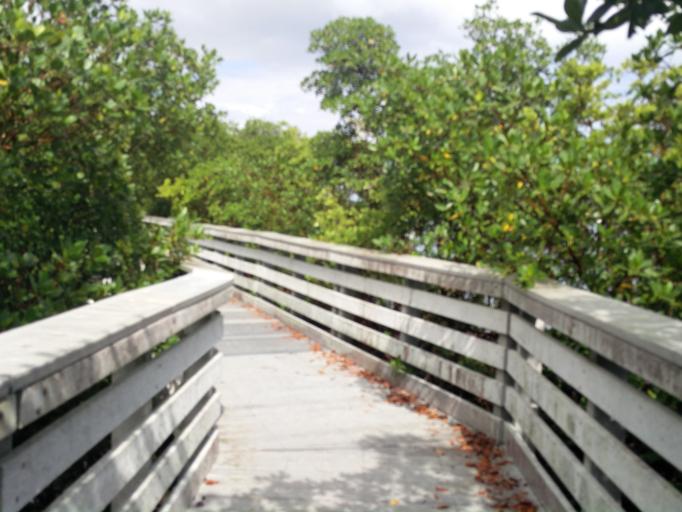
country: US
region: Florida
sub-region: Broward County
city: Dania Beach
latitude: 26.0394
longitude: -80.1179
